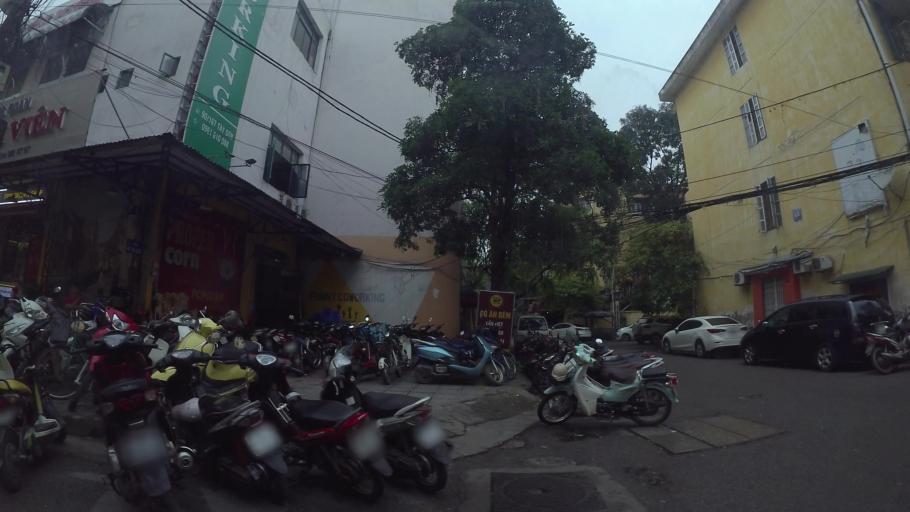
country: VN
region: Ha Noi
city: Dong Da
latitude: 21.0096
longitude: 105.8274
